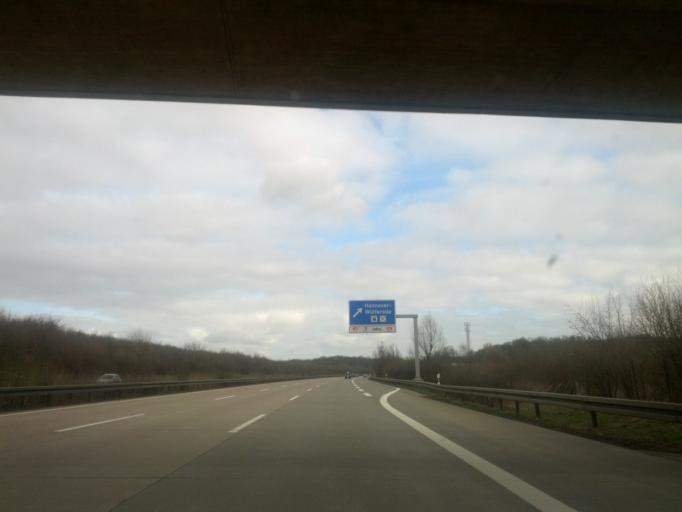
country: DE
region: Lower Saxony
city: Laatzen
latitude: 52.3263
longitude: 9.8634
